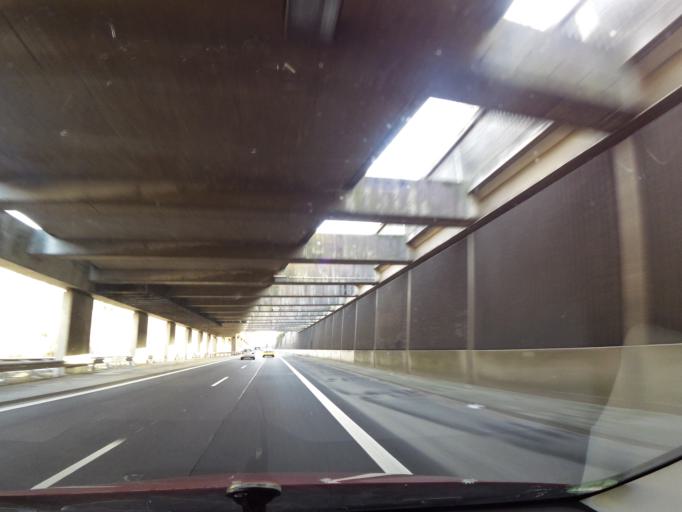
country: DE
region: North Rhine-Westphalia
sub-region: Regierungsbezirk Koln
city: Konigswinter
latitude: 50.7007
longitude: 7.1811
